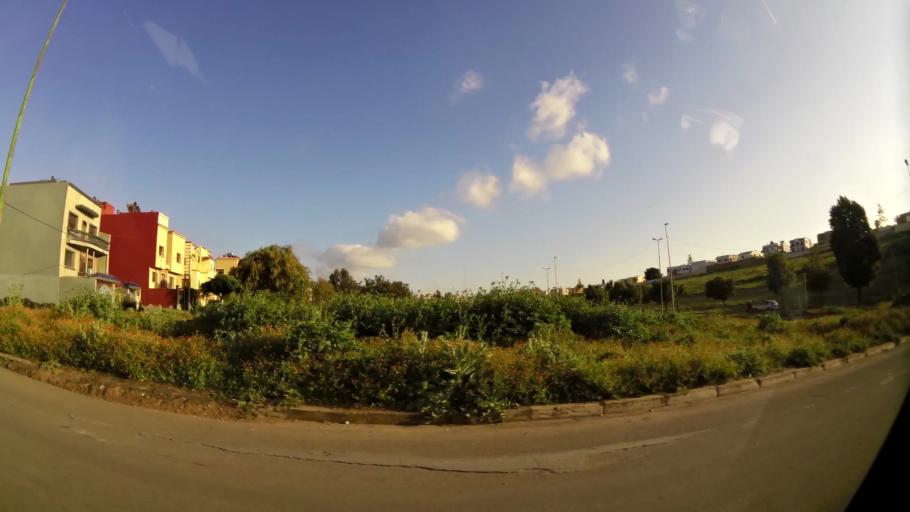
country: MA
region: Chaouia-Ouardigha
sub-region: Settat Province
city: Settat
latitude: 33.0089
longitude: -7.6101
